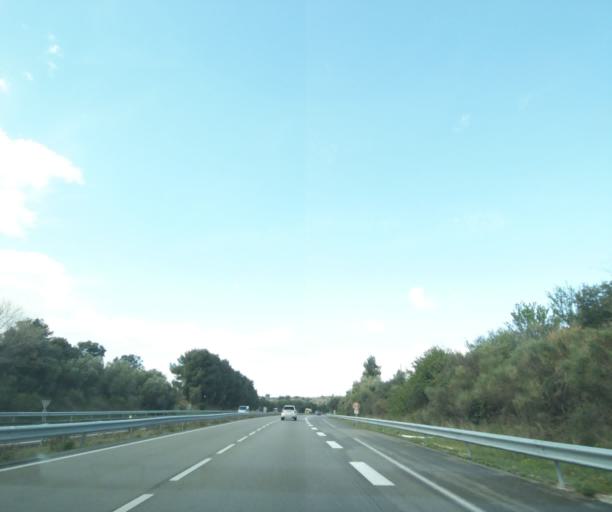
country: FR
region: Languedoc-Roussillon
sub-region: Departement du Gard
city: Roquemaure
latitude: 44.0460
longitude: 4.7649
